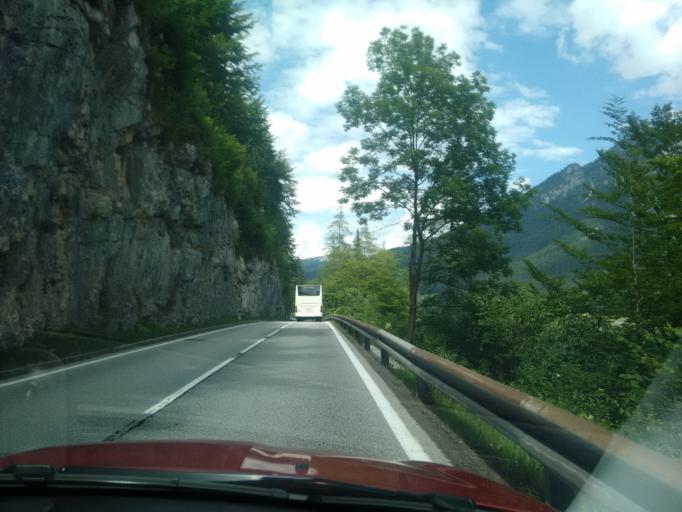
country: AT
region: Upper Austria
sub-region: Politischer Bezirk Gmunden
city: Bad Goisern
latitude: 47.5847
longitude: 13.6573
